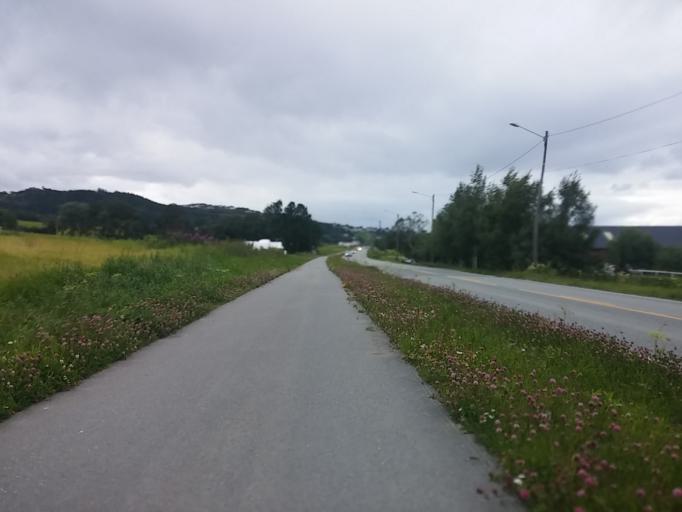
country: NO
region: Sor-Trondelag
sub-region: Malvik
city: Malvik
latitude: 63.4344
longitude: 10.6856
